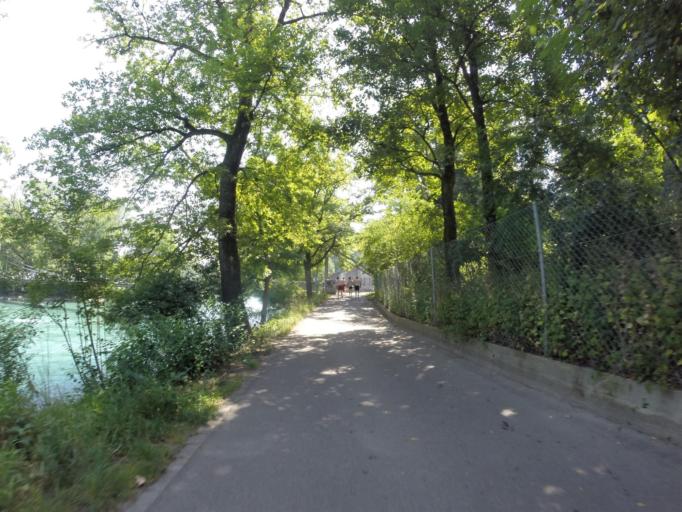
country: CH
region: Bern
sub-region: Bern-Mittelland District
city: Bern
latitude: 46.9347
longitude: 7.4455
